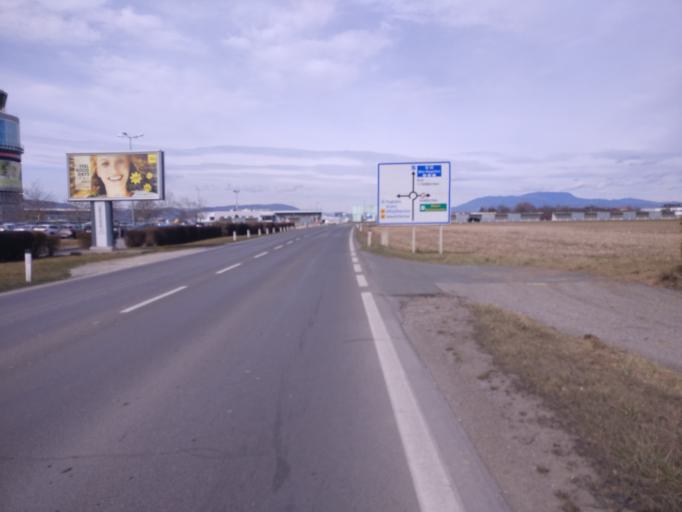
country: AT
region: Styria
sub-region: Politischer Bezirk Graz-Umgebung
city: Feldkirchen bei Graz
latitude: 46.9950
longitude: 15.4476
